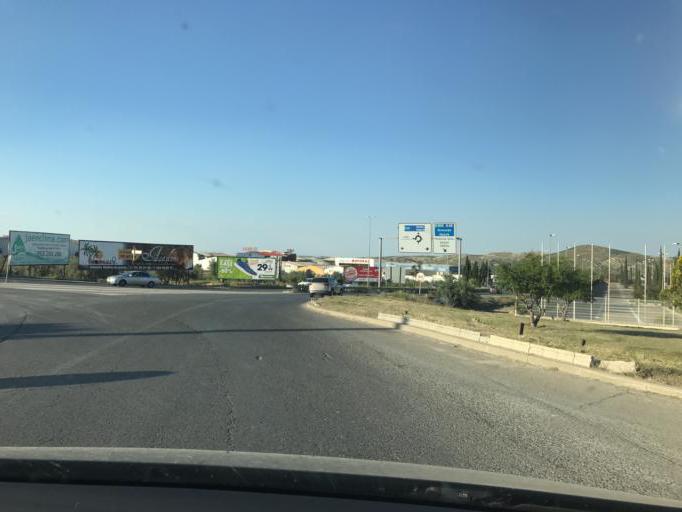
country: ES
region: Andalusia
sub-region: Provincia de Jaen
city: Jaen
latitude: 37.7762
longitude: -3.7587
